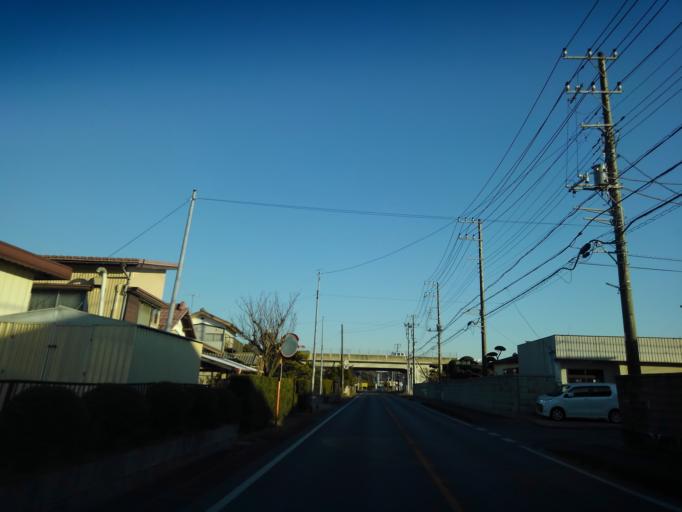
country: JP
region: Chiba
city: Kimitsu
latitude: 35.3086
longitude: 139.9411
